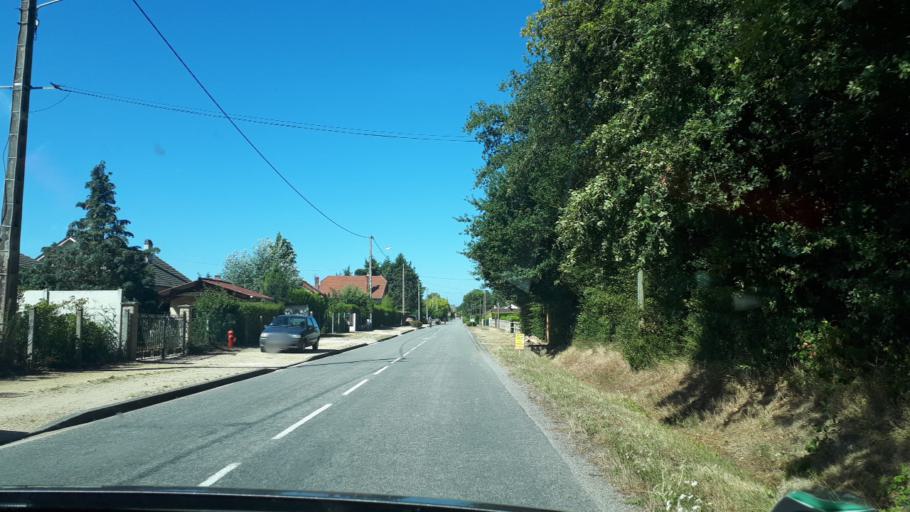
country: FR
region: Centre
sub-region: Departement du Loiret
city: Cerdon
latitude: 47.6371
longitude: 2.3759
